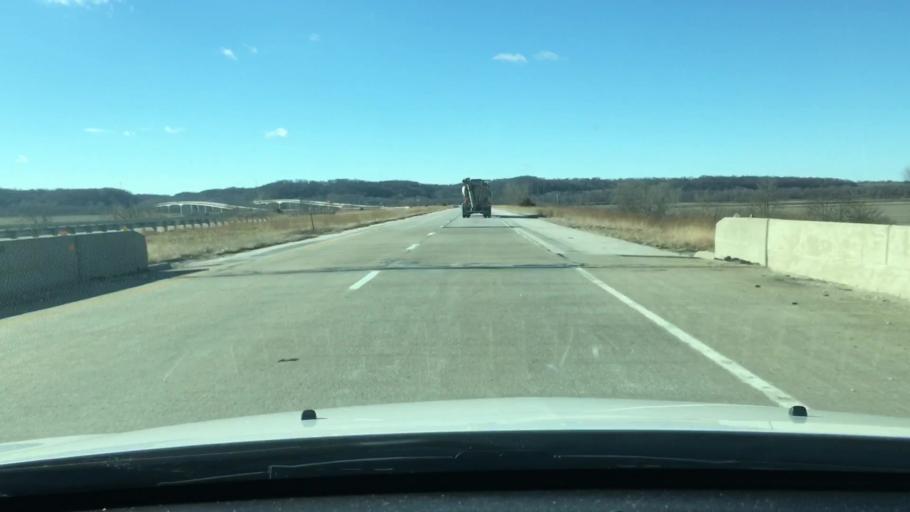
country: US
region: Illinois
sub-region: Pike County
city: Griggsville
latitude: 39.6921
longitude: -90.6198
